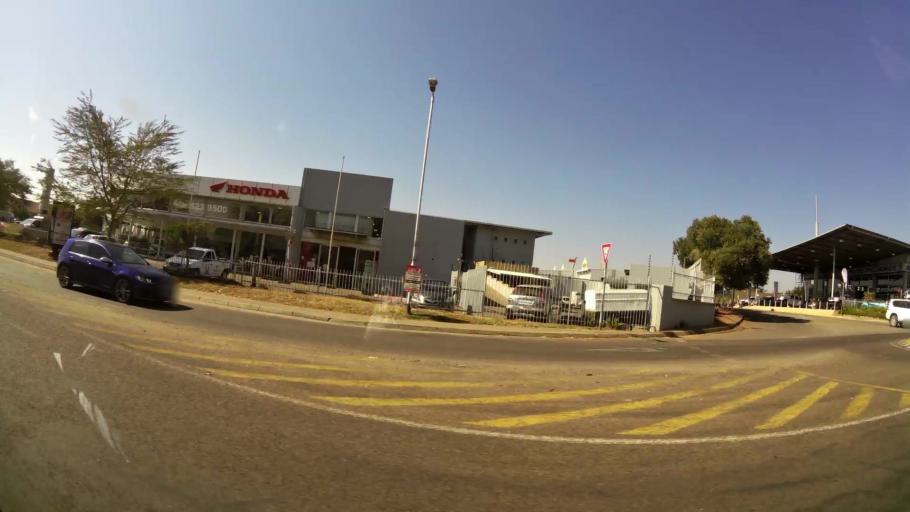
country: ZA
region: Gauteng
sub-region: City of Tshwane Metropolitan Municipality
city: Pretoria
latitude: -25.6834
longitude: 28.2712
